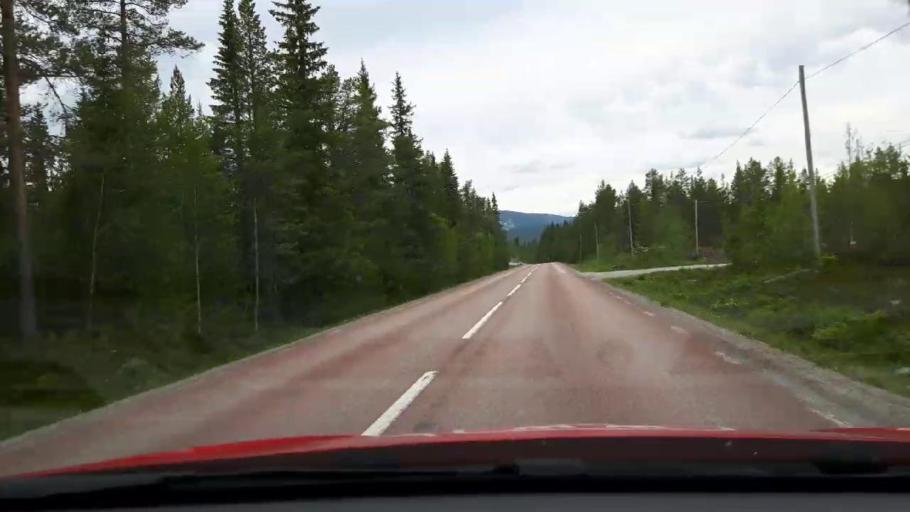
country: NO
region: Hedmark
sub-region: Engerdal
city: Engerdal
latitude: 62.5005
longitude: 12.6274
